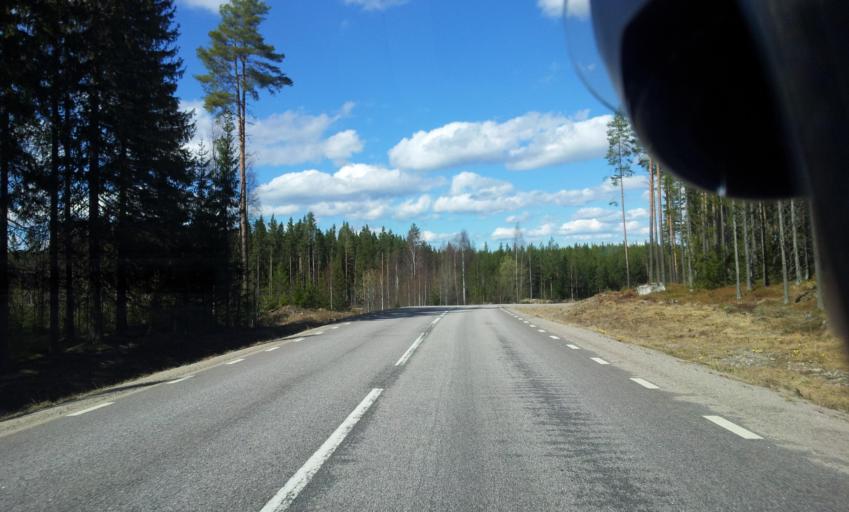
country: SE
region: Gaevleborg
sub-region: Bollnas Kommun
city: Vittsjo
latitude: 61.1450
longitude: 15.8857
